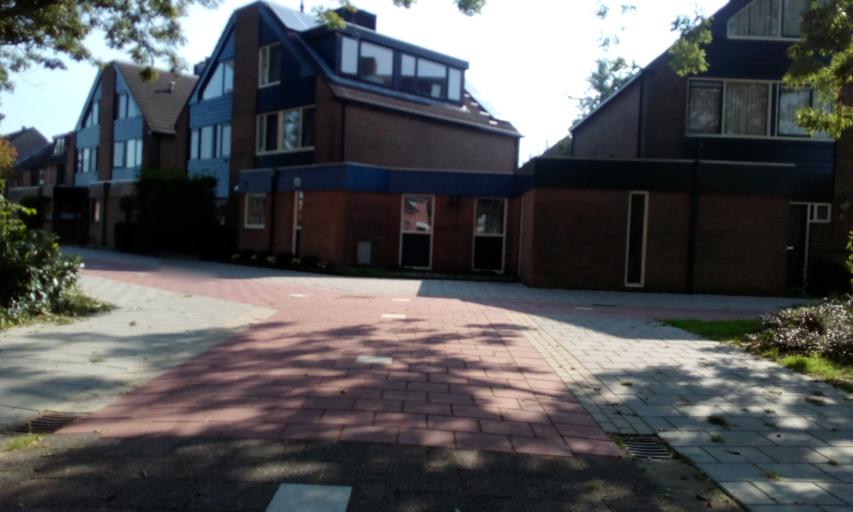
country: NL
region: South Holland
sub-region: Gemeente Capelle aan den IJssel
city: Capelle aan den IJssel
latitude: 51.9744
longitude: 4.6147
